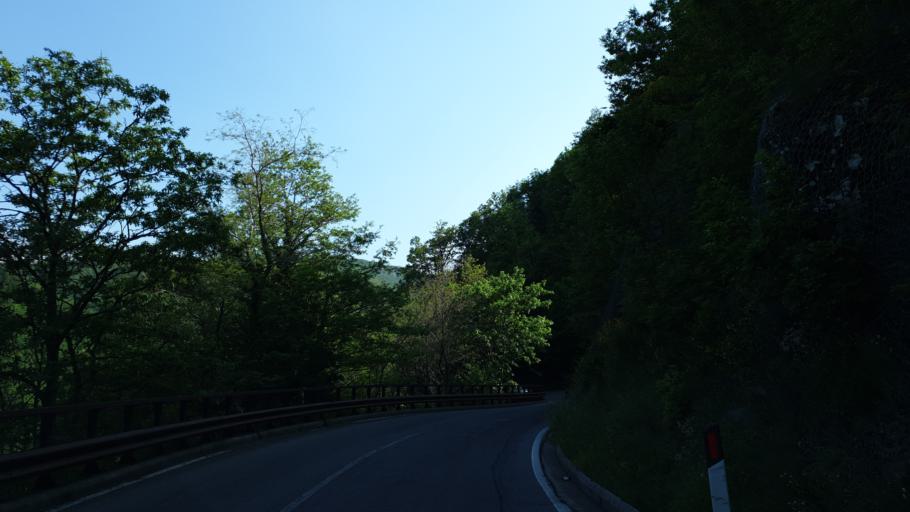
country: IT
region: Tuscany
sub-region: Province of Arezzo
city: Soci
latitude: 43.7812
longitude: 11.8695
